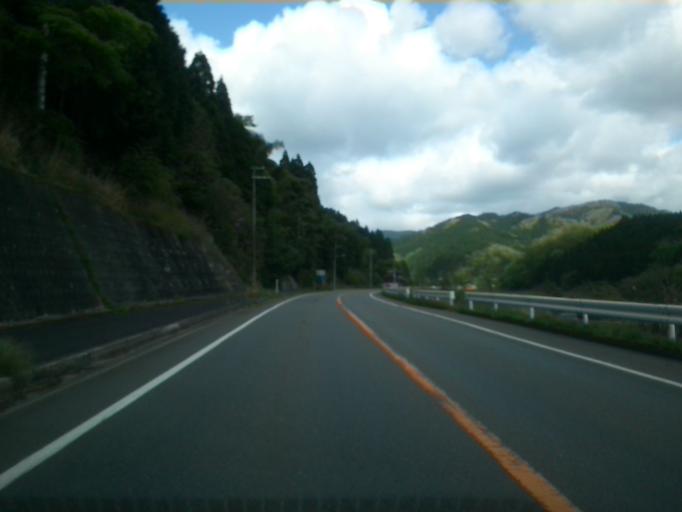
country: JP
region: Kyoto
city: Fukuchiyama
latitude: 35.4190
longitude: 135.0180
